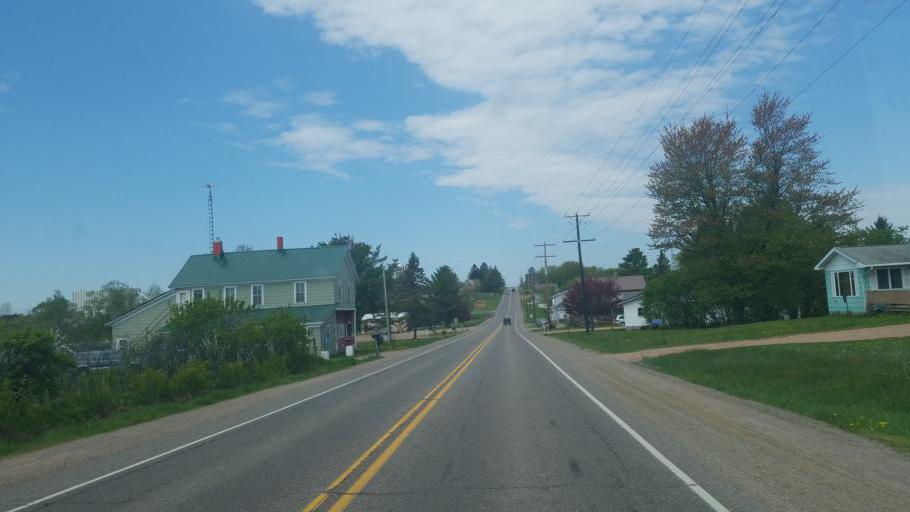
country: US
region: Wisconsin
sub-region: Clark County
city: Loyal
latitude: 44.5823
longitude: -90.4033
